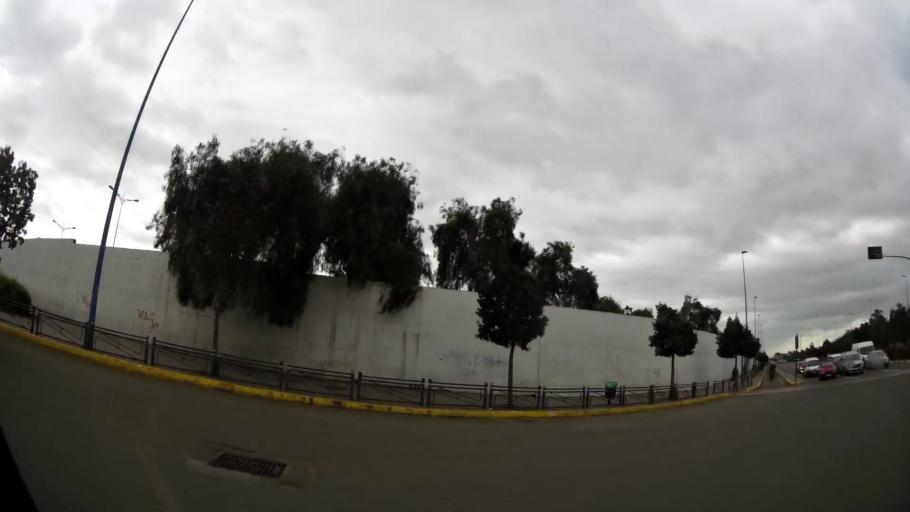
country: MA
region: Grand Casablanca
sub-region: Casablanca
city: Casablanca
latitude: 33.5566
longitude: -7.5589
